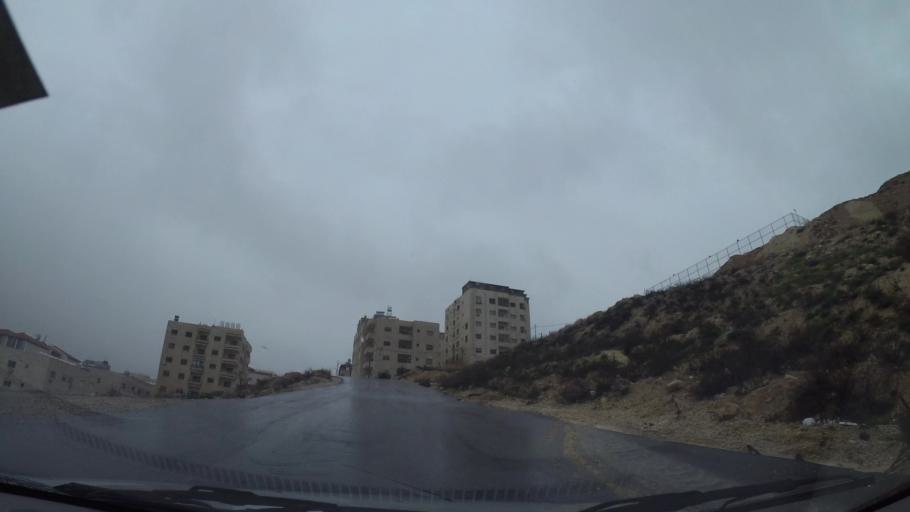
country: JO
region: Amman
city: Al Jubayhah
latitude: 32.0219
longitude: 35.8886
